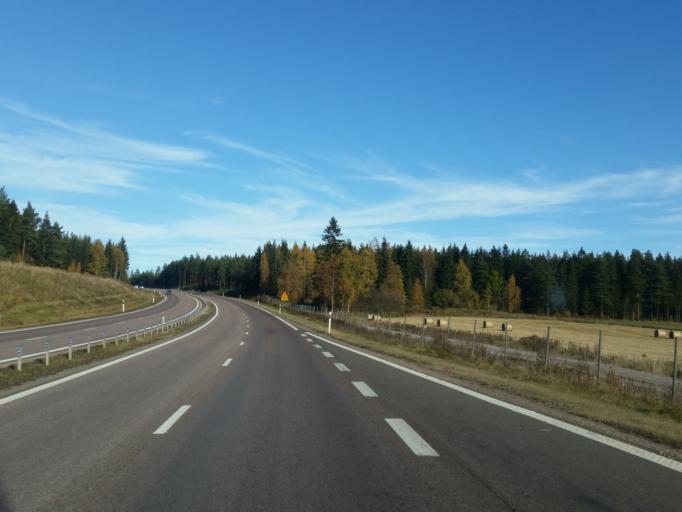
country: SE
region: Dalarna
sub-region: Borlange Kommun
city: Ornas
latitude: 60.5175
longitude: 15.5496
